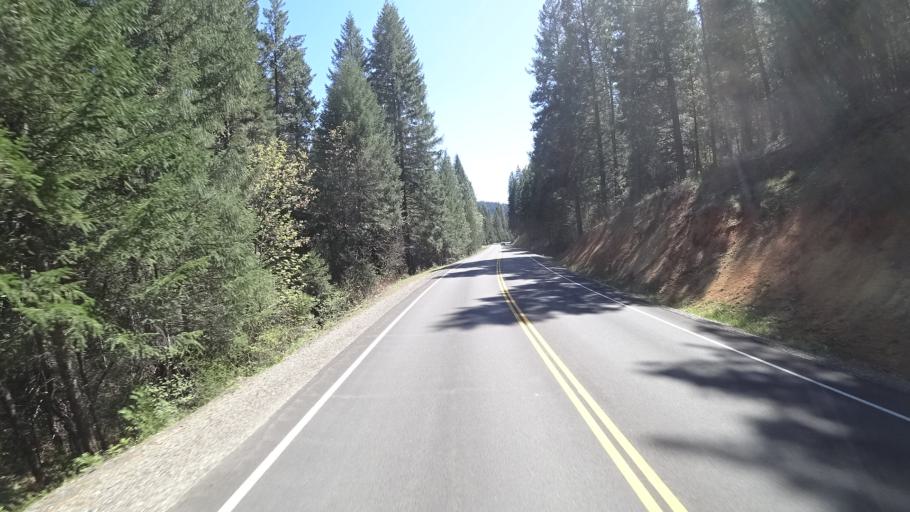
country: US
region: California
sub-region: Trinity County
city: Lewiston
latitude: 40.9001
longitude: -122.7864
